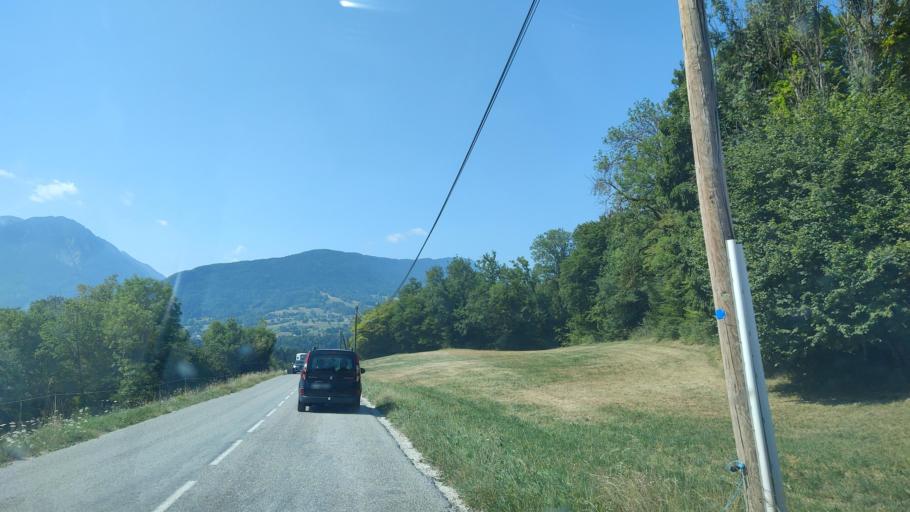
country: FR
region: Rhone-Alpes
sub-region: Departement de la Haute-Savoie
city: Gruffy
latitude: 45.7332
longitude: 6.1104
